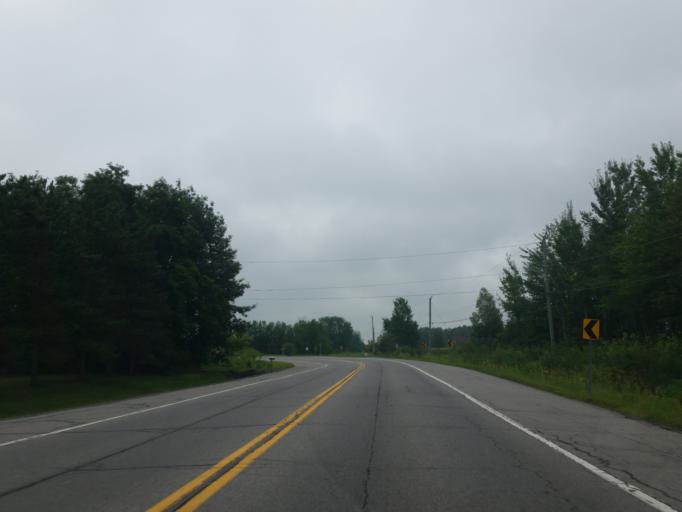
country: CA
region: Ontario
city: Clarence-Rockland
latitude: 45.3424
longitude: -75.3641
